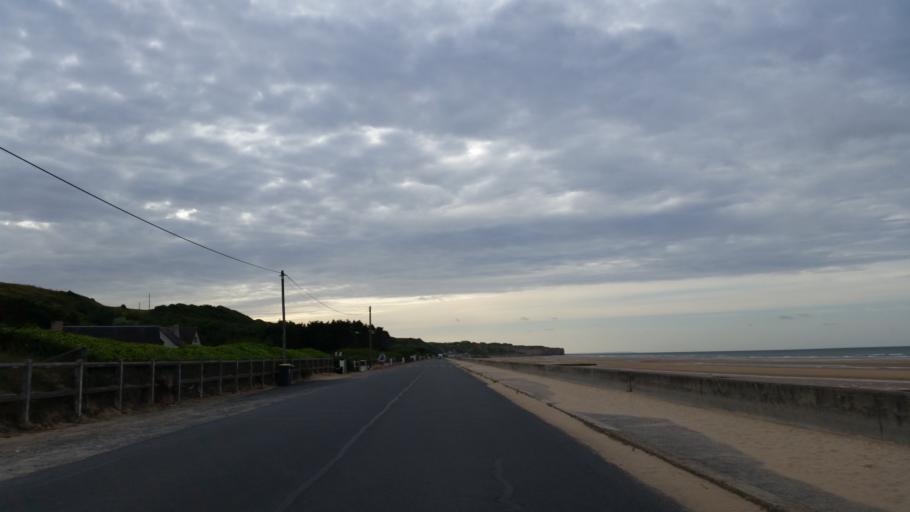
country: FR
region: Lower Normandy
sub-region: Departement du Calvados
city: Le Molay-Littry
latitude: 49.3722
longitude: -0.8838
